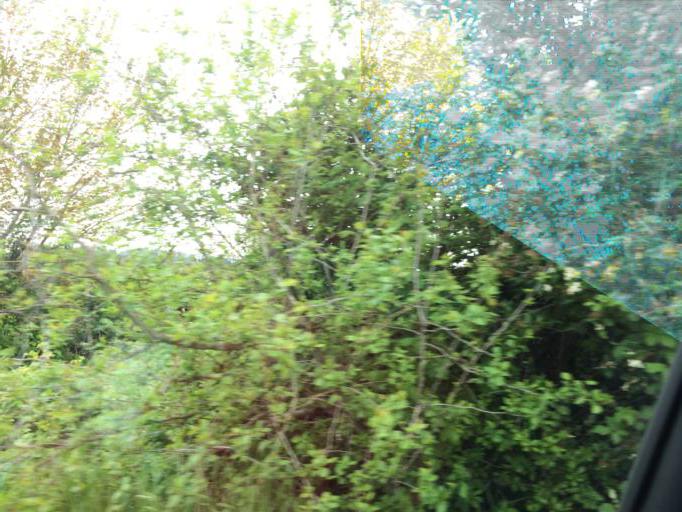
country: CA
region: British Columbia
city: Ladner
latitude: 49.1318
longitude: -123.1033
